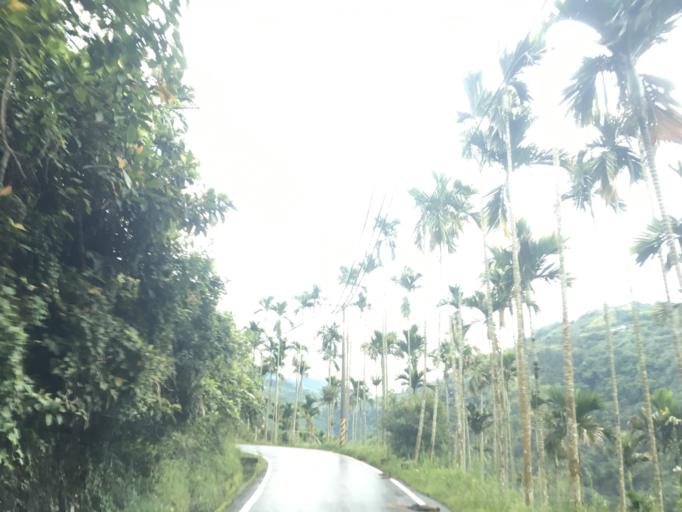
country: TW
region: Taiwan
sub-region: Yunlin
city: Douliu
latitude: 23.5609
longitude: 120.6525
